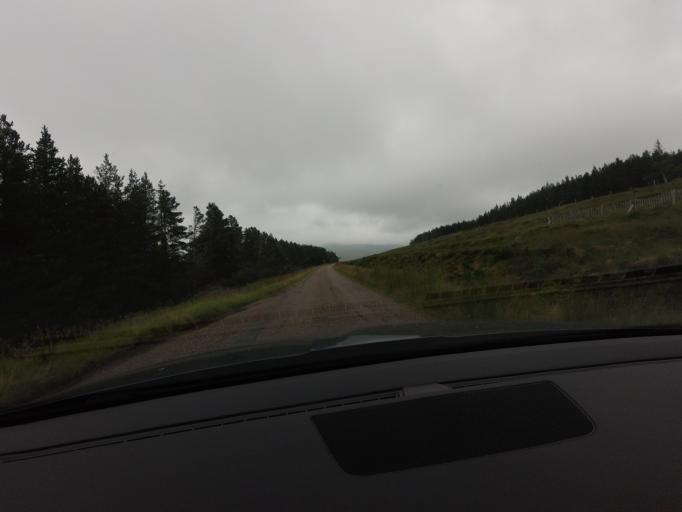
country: GB
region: Scotland
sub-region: Highland
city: Golspie
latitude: 58.3425
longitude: -4.4358
